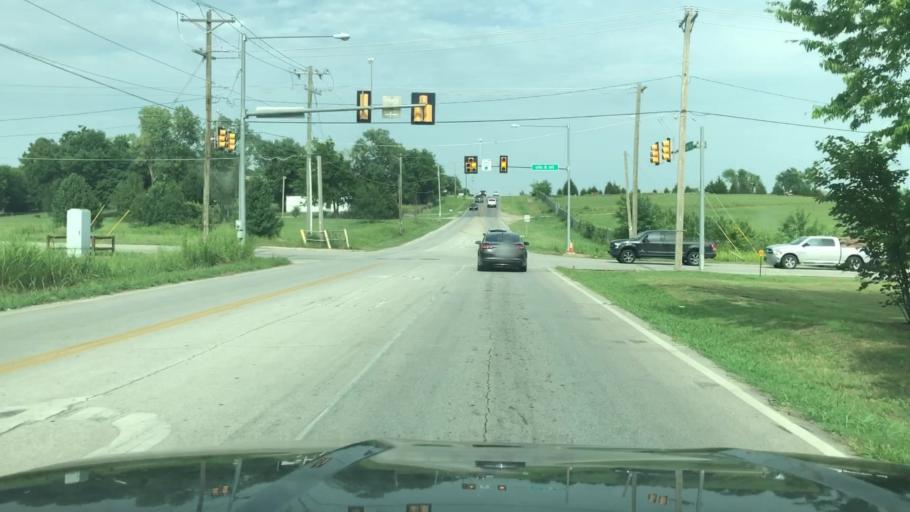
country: US
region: Oklahoma
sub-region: Tulsa County
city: Oakhurst
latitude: 36.0900
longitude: -96.0659
